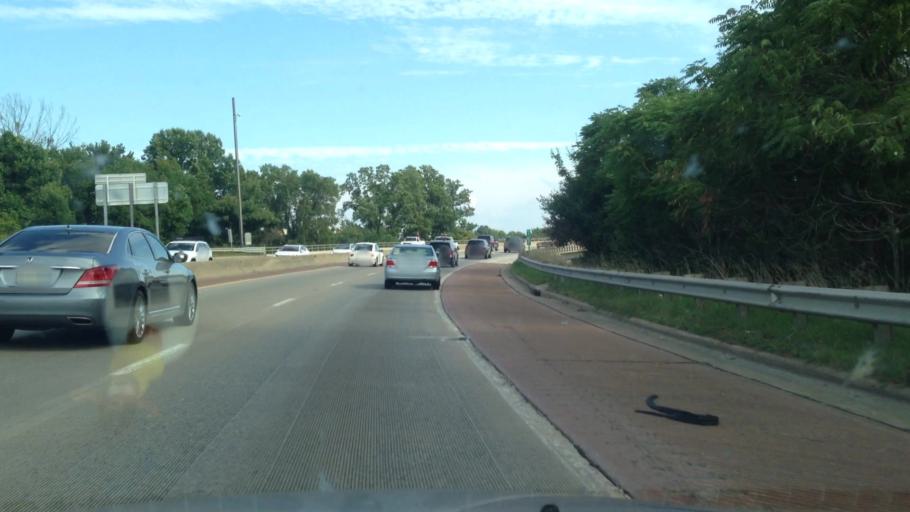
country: US
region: North Carolina
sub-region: Forsyth County
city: Winston-Salem
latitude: 36.0729
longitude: -80.2290
